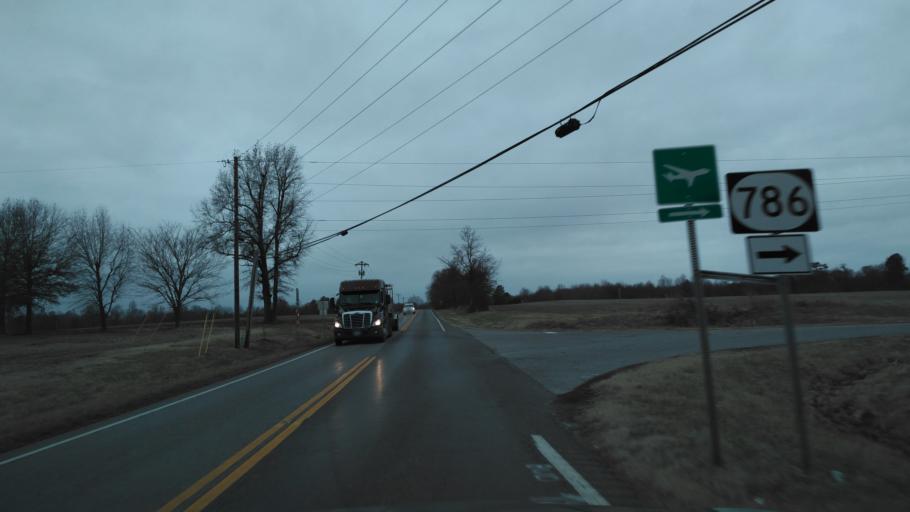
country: US
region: Kentucky
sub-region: McCracken County
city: Massac
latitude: 37.0341
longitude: -88.7412
